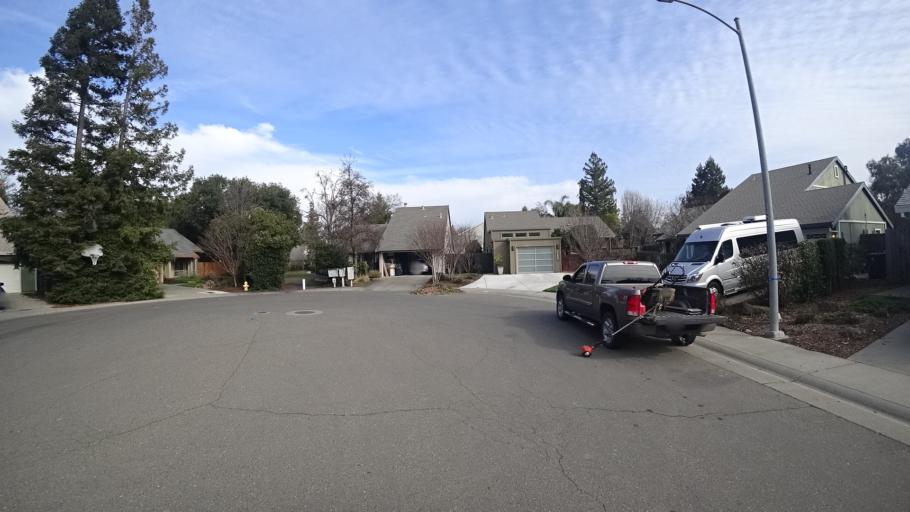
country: US
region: California
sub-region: Yolo County
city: Davis
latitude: 38.5429
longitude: -121.7198
